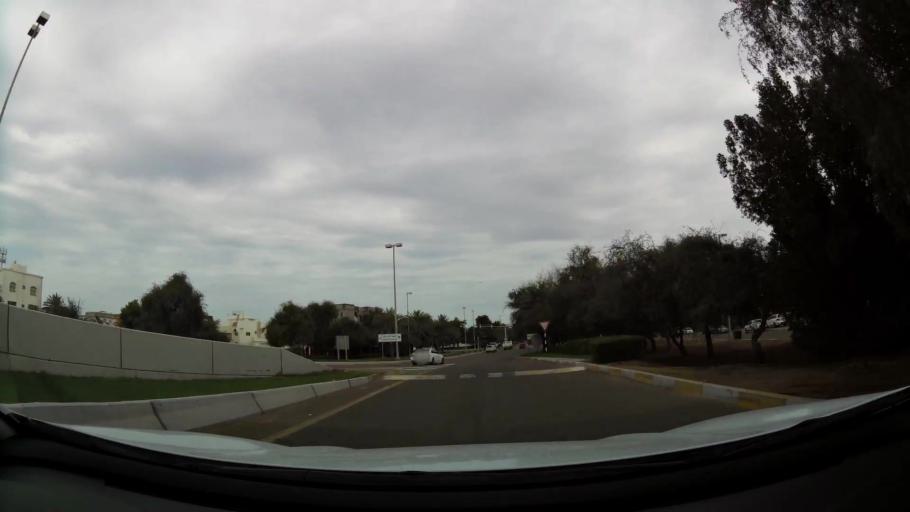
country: AE
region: Abu Dhabi
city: Abu Dhabi
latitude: 24.4239
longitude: 54.4175
